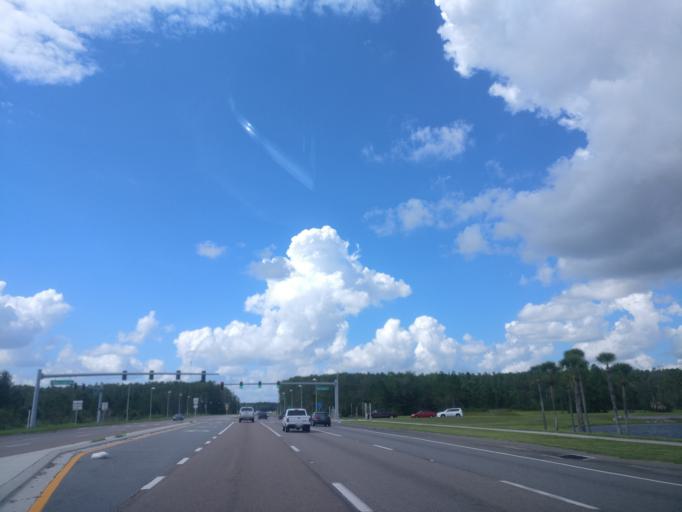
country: US
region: Florida
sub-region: Orange County
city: Hunters Creek
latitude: 28.3471
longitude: -81.4039
